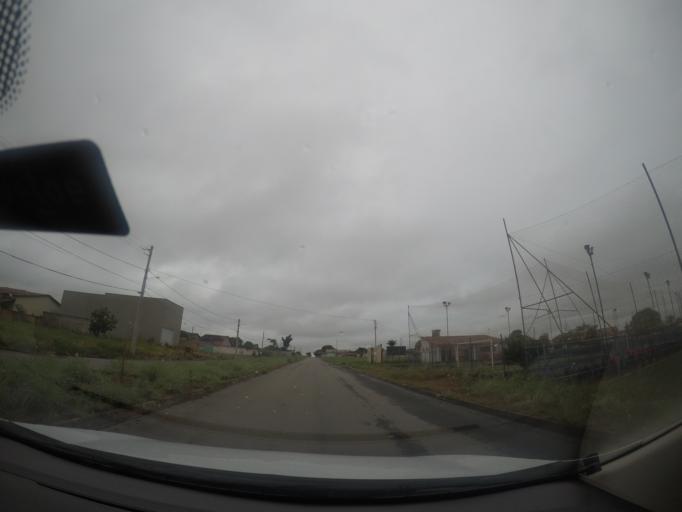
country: BR
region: Goias
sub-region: Goiania
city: Goiania
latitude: -16.7554
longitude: -49.3176
